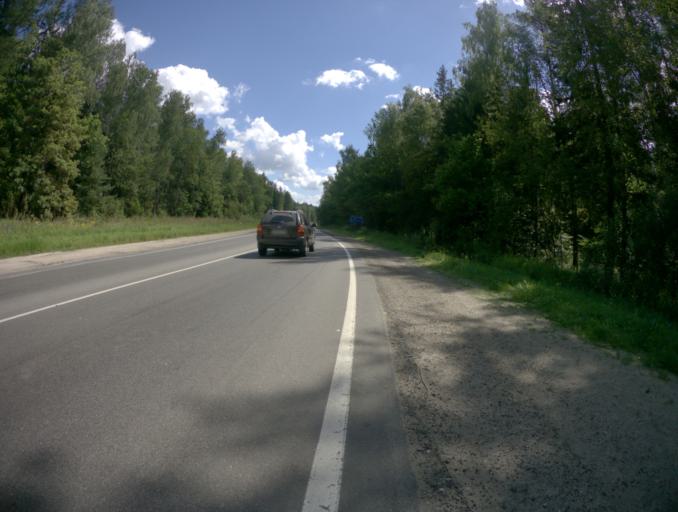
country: RU
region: Vladimir
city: Kommunar
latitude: 56.0211
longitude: 40.5759
